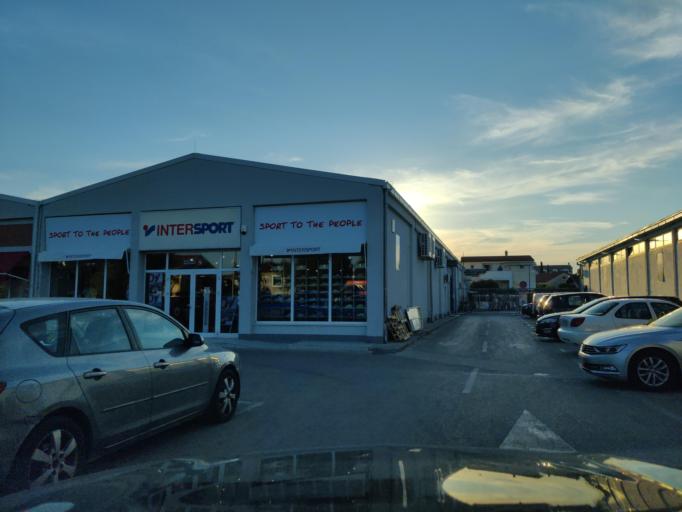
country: HR
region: Sibensko-Kniniska
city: Vodice
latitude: 43.7602
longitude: 15.7831
